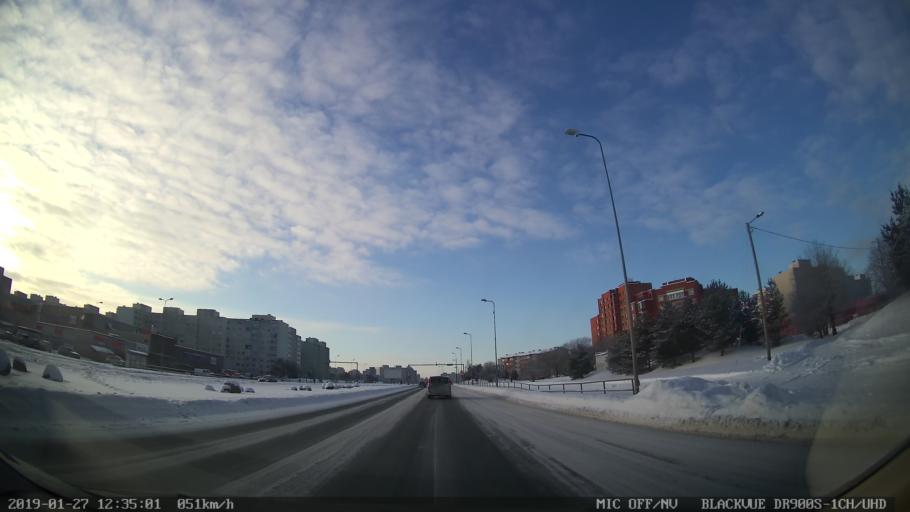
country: EE
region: Harju
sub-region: Tallinna linn
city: Kose
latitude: 59.4453
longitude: 24.8905
